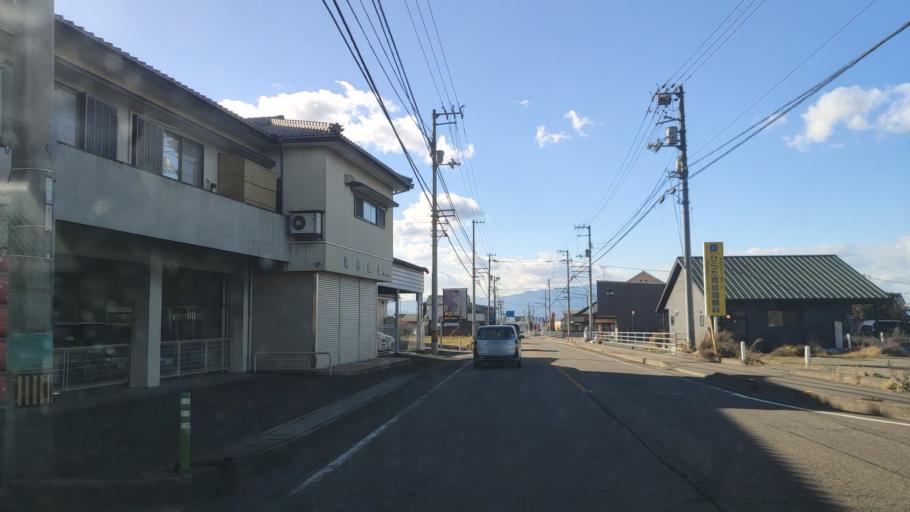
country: JP
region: Ehime
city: Saijo
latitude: 33.9187
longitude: 133.2274
